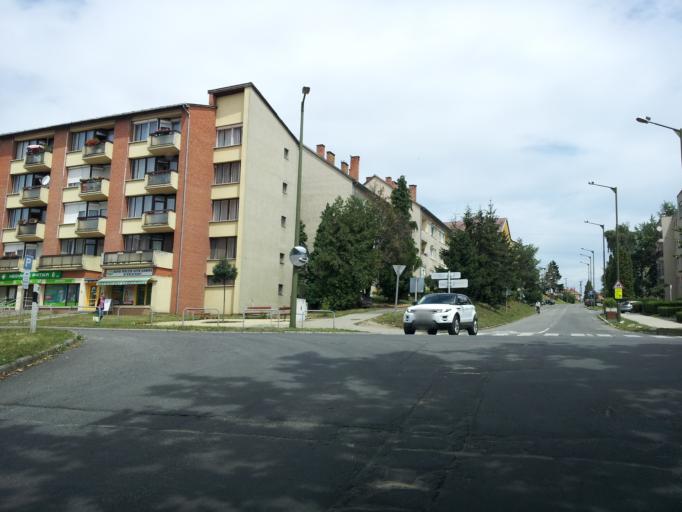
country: HU
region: Vas
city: Vasvar
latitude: 47.0484
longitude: 16.8018
